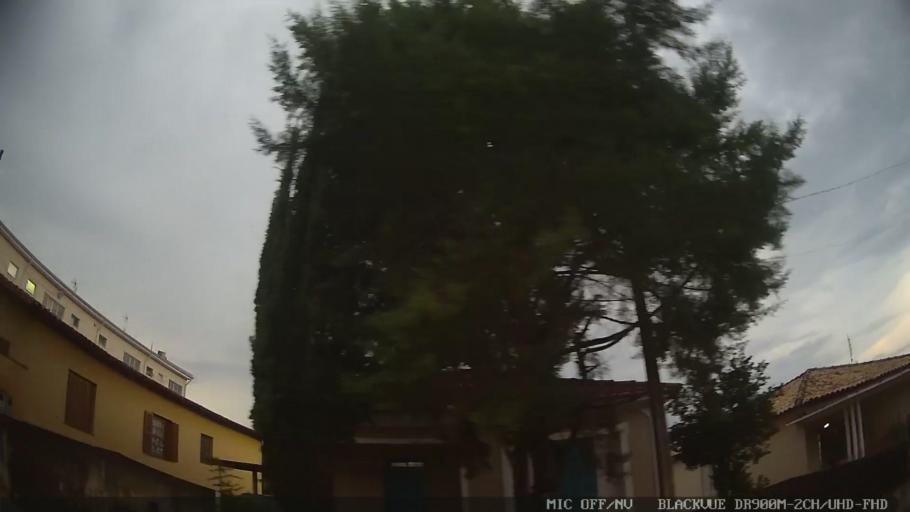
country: BR
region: Sao Paulo
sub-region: Itatiba
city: Itatiba
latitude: -22.8771
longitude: -46.7909
